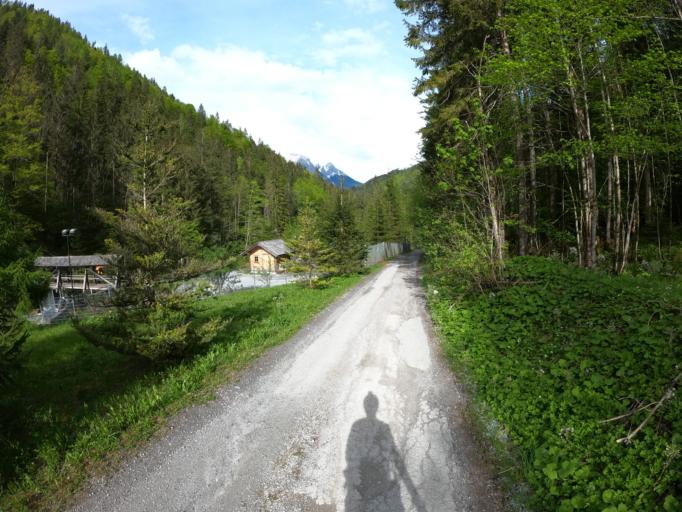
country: AT
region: Salzburg
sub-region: Politischer Bezirk Sankt Johann im Pongau
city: Werfen
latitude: 47.4777
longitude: 13.1351
